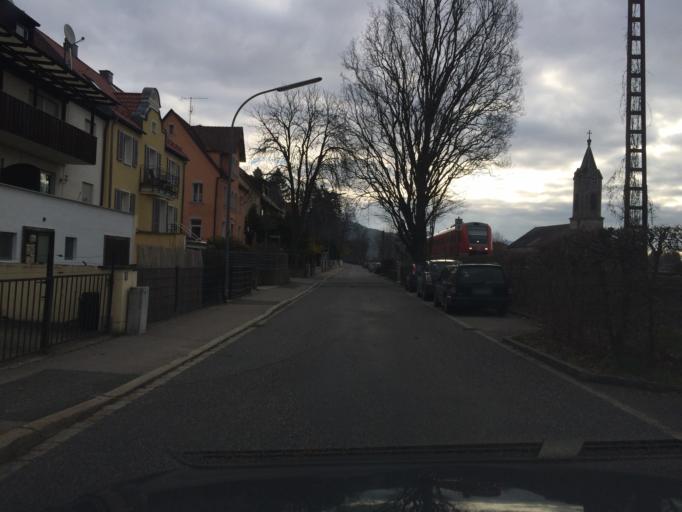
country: DE
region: Bavaria
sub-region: Regierungsbezirk Mittelfranken
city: Hersbruck
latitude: 49.5116
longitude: 11.4316
